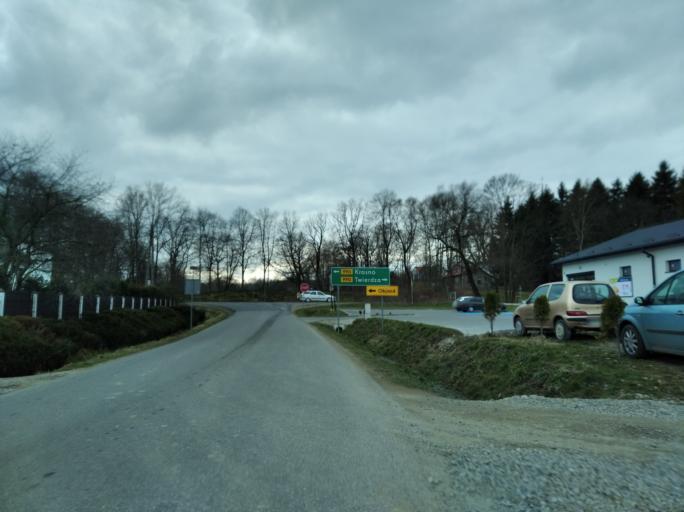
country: PL
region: Subcarpathian Voivodeship
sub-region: Powiat krosnienski
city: Odrzykon
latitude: 49.7476
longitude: 21.7024
